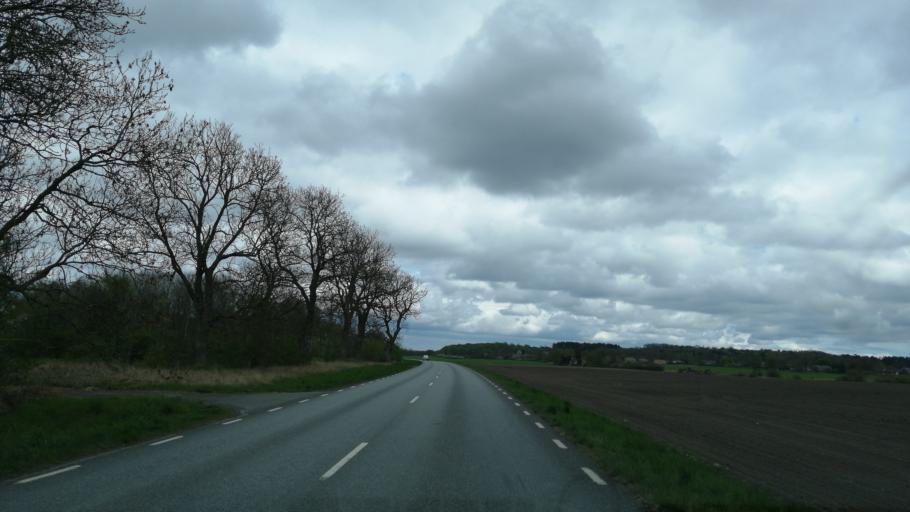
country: SE
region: Skane
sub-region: Kristianstads Kommun
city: Fjalkinge
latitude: 56.0694
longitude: 14.3390
